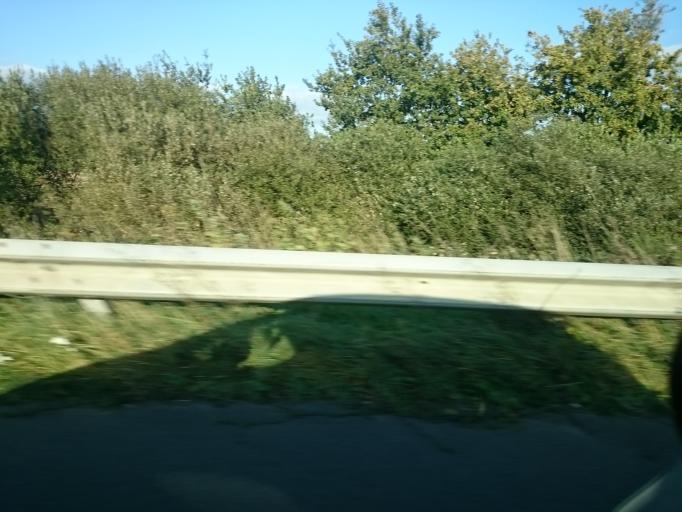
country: FR
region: Pays de la Loire
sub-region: Departement de la Loire-Atlantique
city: Derval
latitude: 47.6622
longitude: -1.6804
